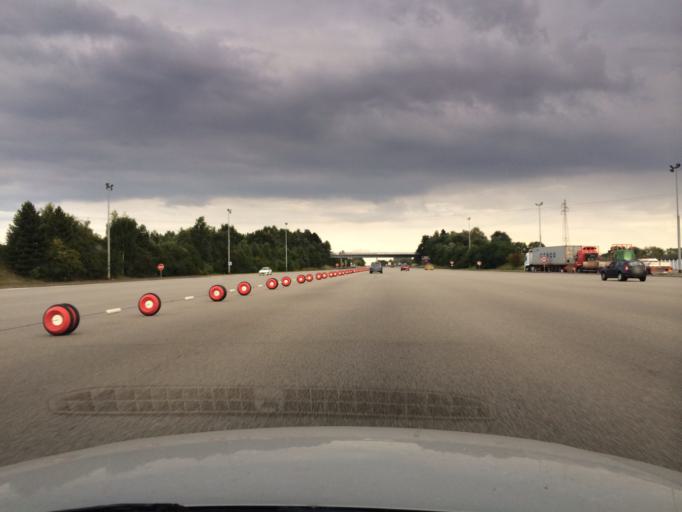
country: FR
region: Haute-Normandie
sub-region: Departement de l'Eure
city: Ande
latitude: 49.1910
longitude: 1.2327
